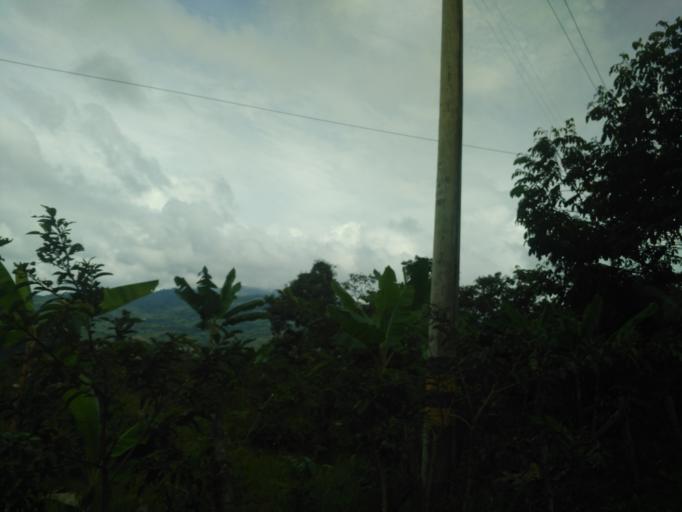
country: CO
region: Valle del Cauca
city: Sevilla
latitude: 4.2942
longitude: -75.9006
